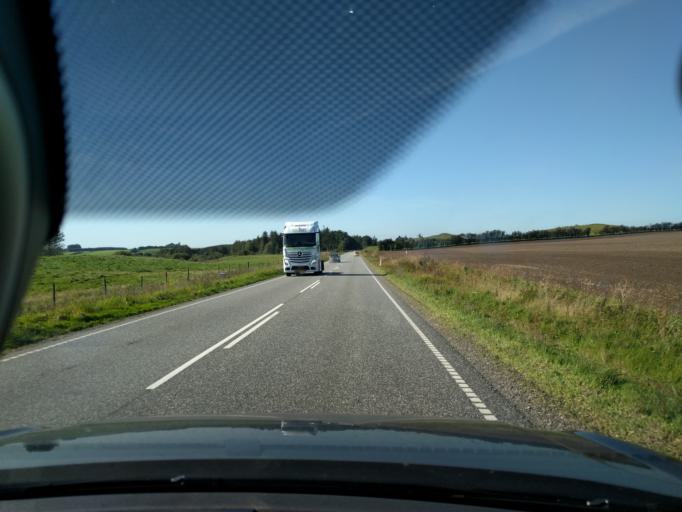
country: DK
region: North Denmark
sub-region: Mariagerfjord Kommune
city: Hobro
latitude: 56.6690
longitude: 9.7123
